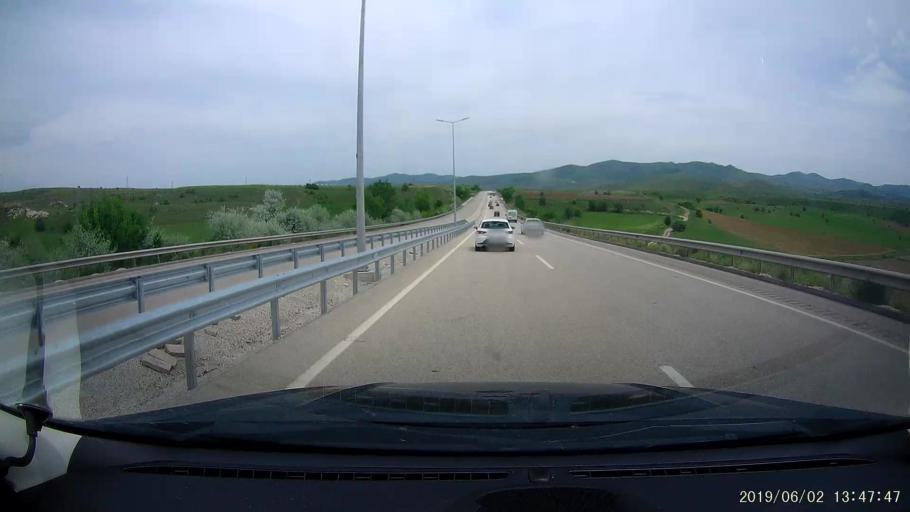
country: TR
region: Cankiri
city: Kursunlu
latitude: 40.8384
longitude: 33.2906
